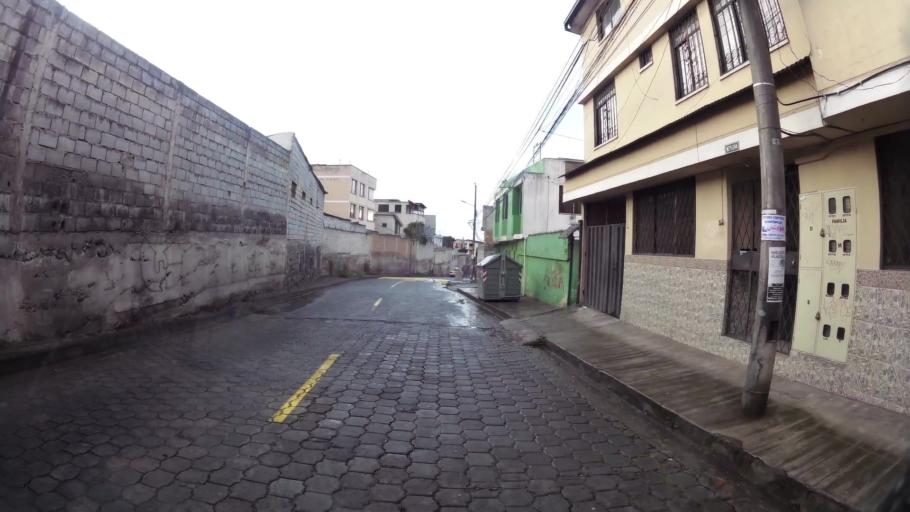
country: EC
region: Pichincha
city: Quito
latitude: -0.1051
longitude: -78.4900
